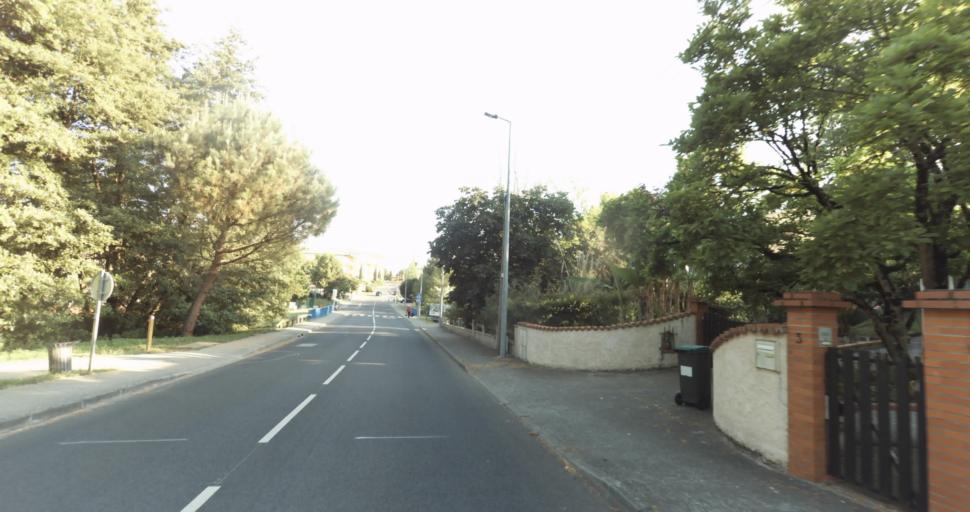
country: FR
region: Midi-Pyrenees
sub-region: Departement de la Haute-Garonne
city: Leguevin
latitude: 43.5963
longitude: 1.2348
